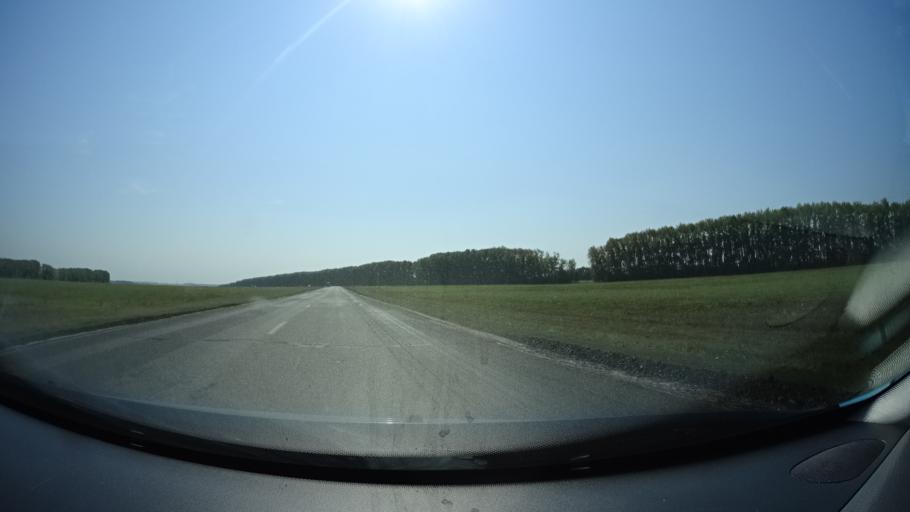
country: RU
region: Bashkortostan
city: Kabakovo
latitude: 54.4544
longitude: 55.9710
